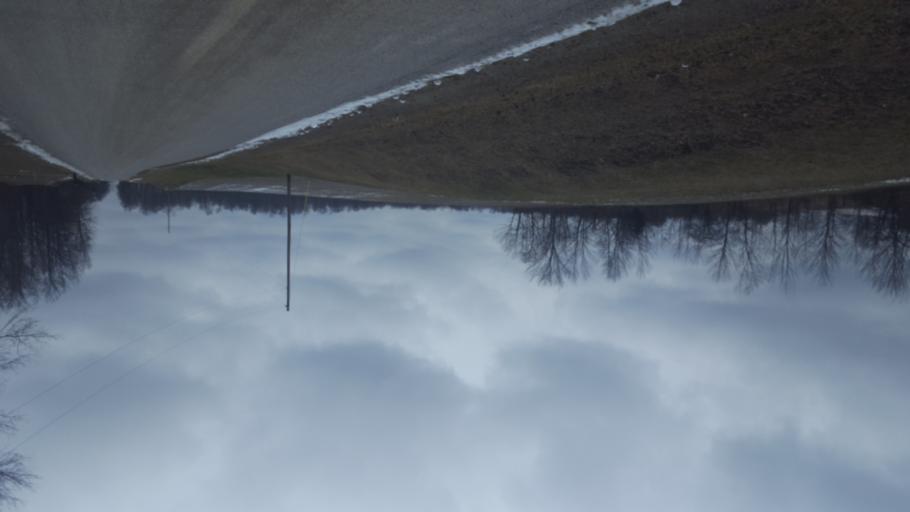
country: US
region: Ohio
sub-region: Crawford County
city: Galion
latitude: 40.6530
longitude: -82.7089
